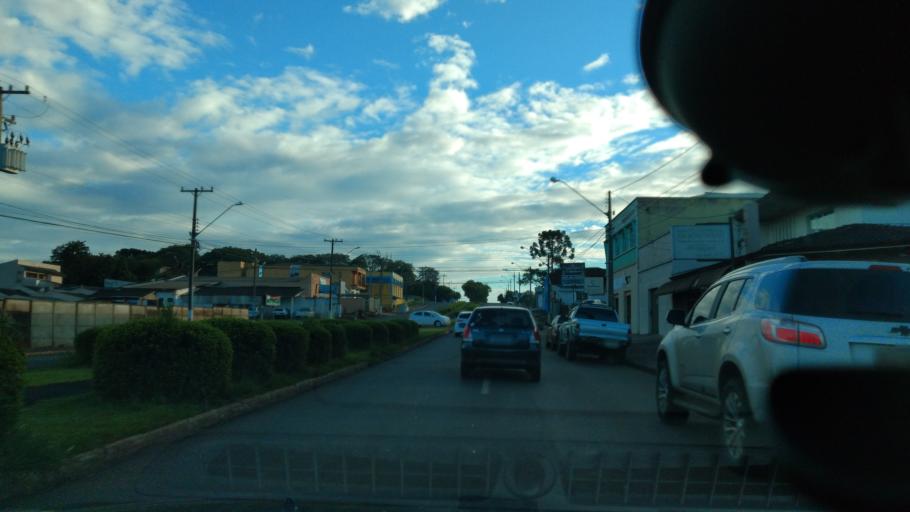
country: BR
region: Parana
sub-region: Guarapuava
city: Guarapuava
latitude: -25.3926
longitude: -51.4801
